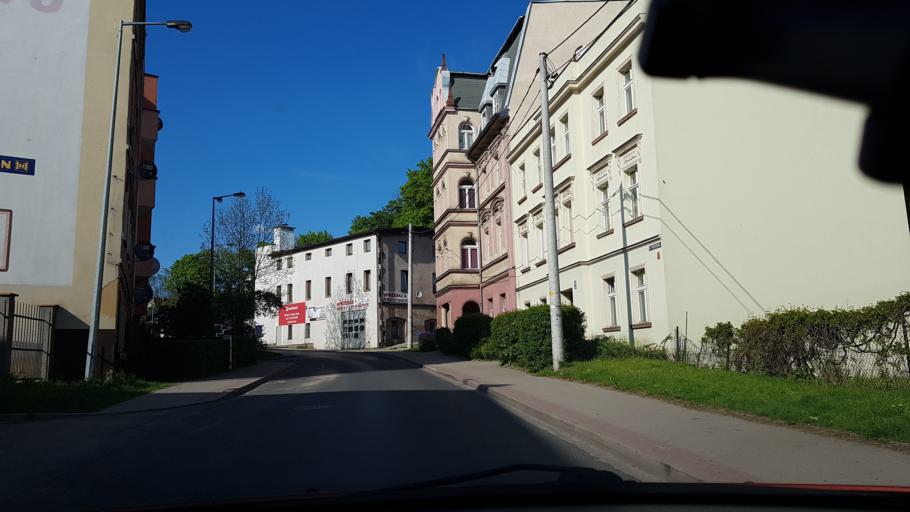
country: PL
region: Lower Silesian Voivodeship
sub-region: Powiat klodzki
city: Nowa Ruda
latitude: 50.5828
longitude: 16.5022
